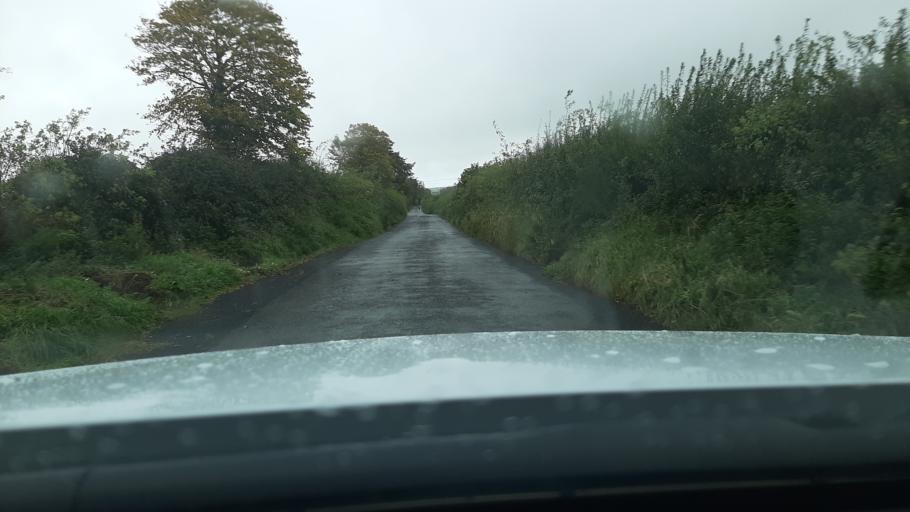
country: IE
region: Leinster
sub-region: Kildare
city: Kildare
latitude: 53.1758
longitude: -6.9243
